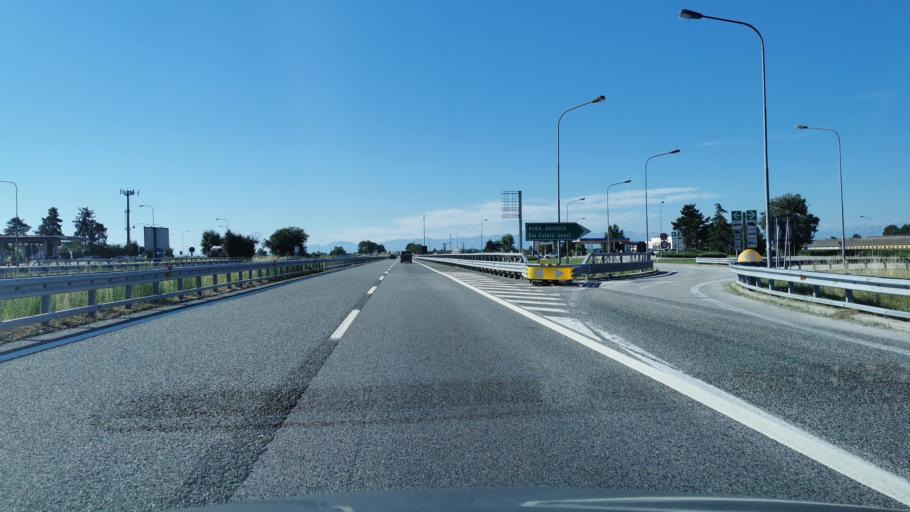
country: IT
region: Piedmont
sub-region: Provincia di Cuneo
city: Marene
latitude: 44.7057
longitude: 7.7630
